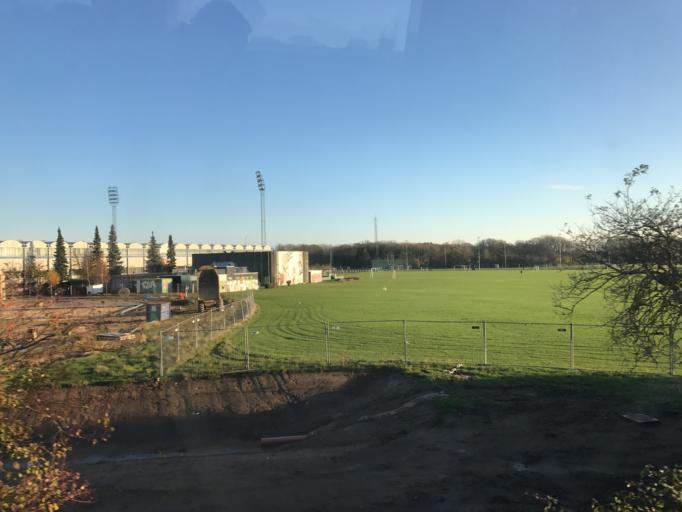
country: DK
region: Capital Region
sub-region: Hvidovre Kommune
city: Hvidovre
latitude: 55.6474
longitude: 12.5082
